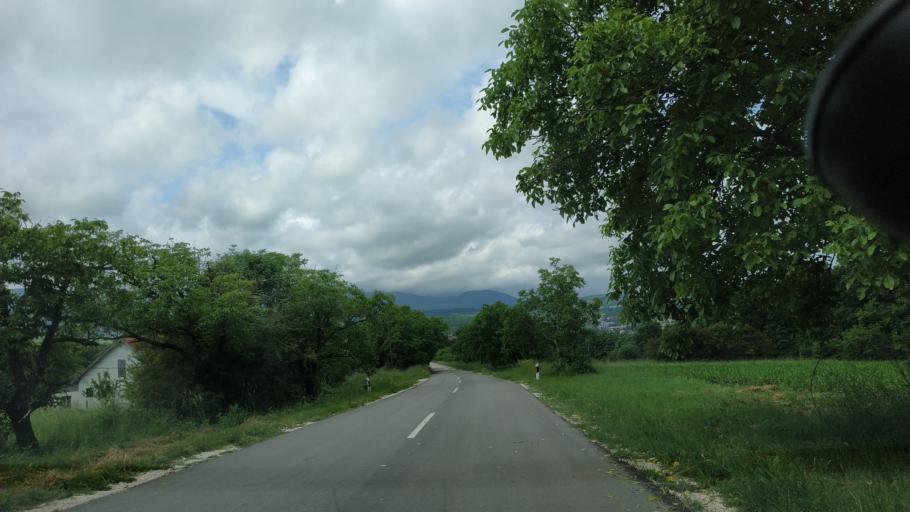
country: RS
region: Central Serbia
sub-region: Zajecarski Okrug
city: Boljevac
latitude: 43.8327
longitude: 21.9749
